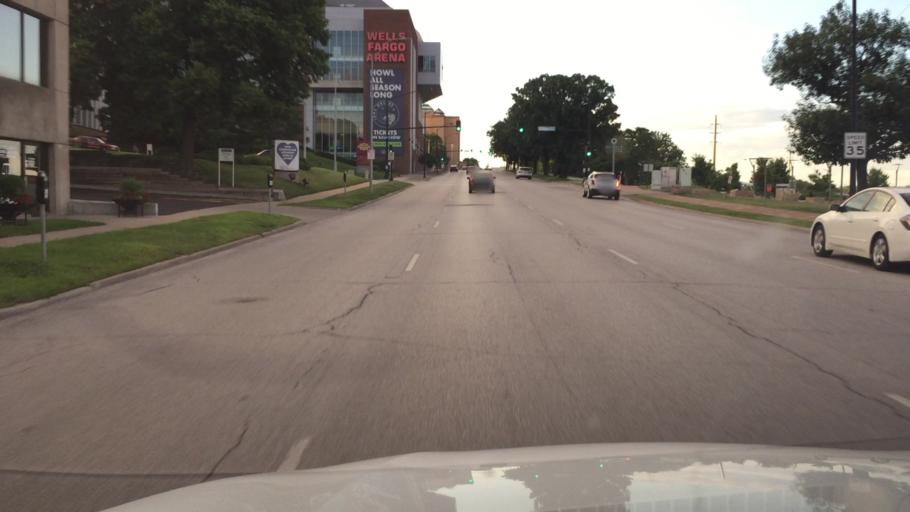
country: US
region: Iowa
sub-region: Polk County
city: Des Moines
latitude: 41.5908
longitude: -93.6204
